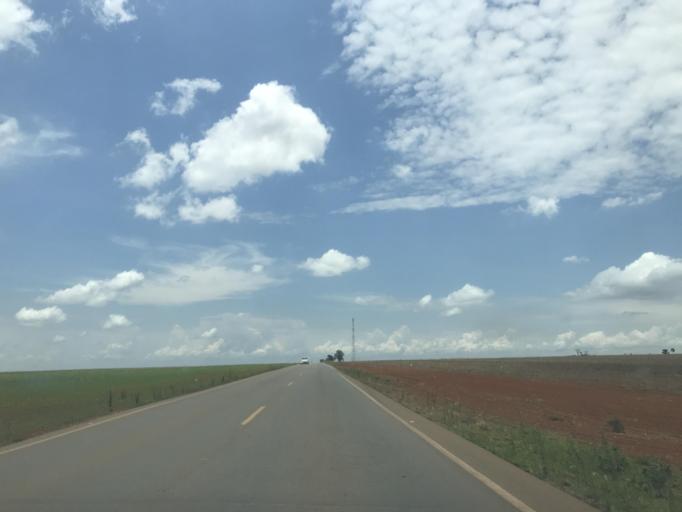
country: BR
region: Goias
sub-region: Vianopolis
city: Vianopolis
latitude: -16.5300
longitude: -48.2448
